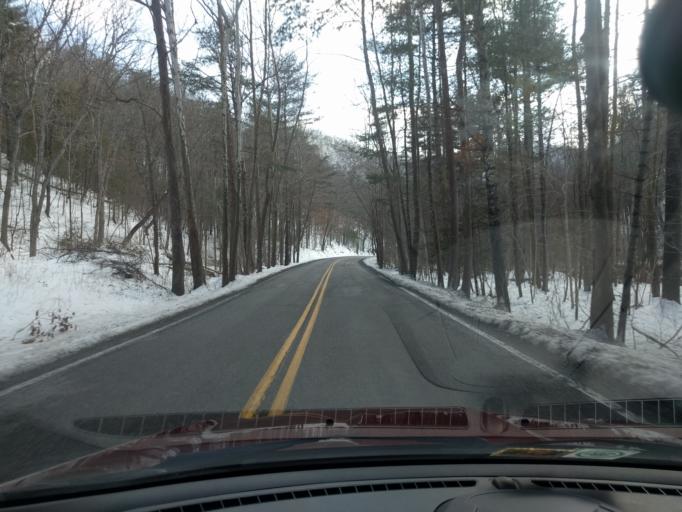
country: US
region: Virginia
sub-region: Bath County
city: Warm Springs
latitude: 38.1238
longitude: -79.9208
